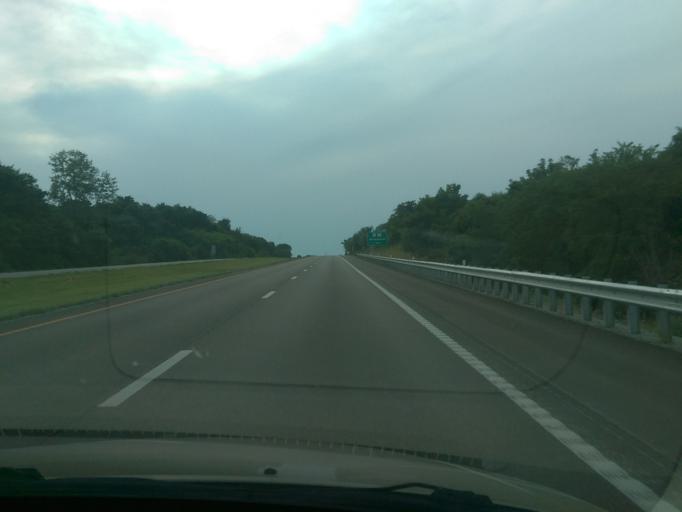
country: US
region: Missouri
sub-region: Andrew County
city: Savannah
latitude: 39.9066
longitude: -94.8890
